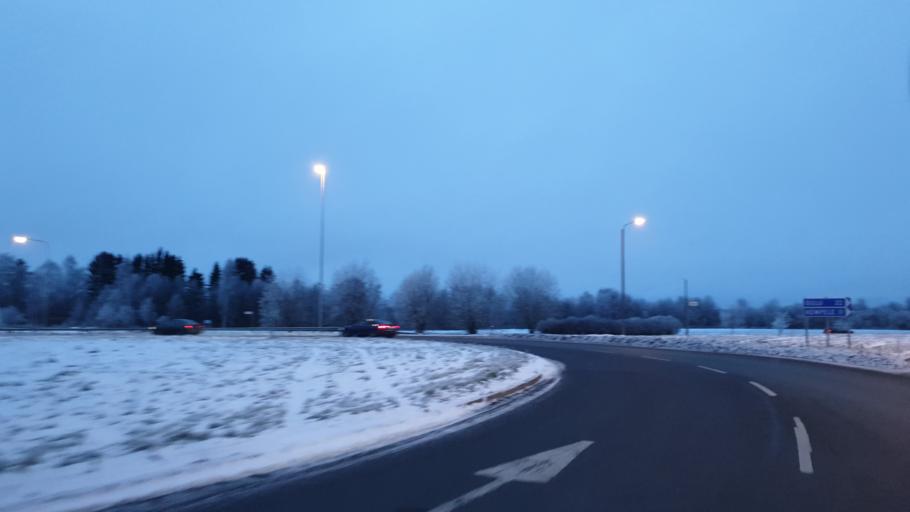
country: FI
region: Northern Ostrobothnia
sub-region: Oulu
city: Liminka
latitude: 64.8154
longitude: 25.4851
